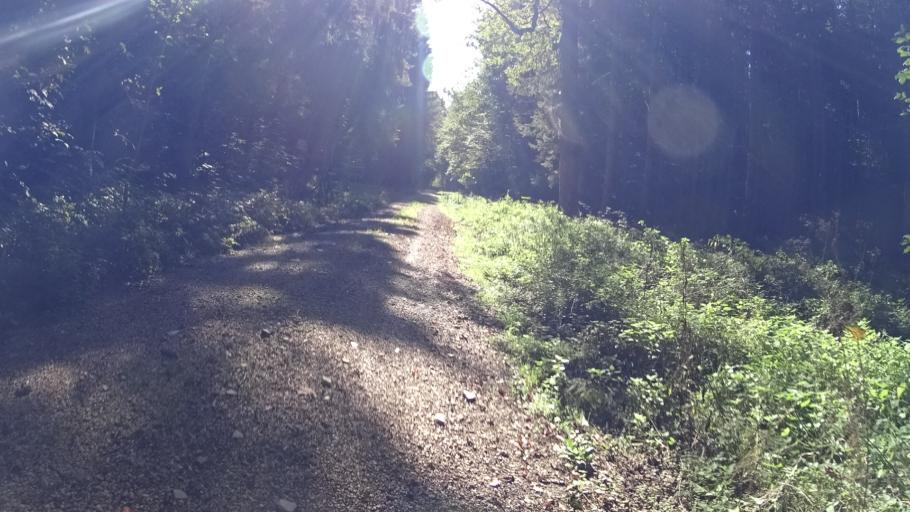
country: DE
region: Bavaria
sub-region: Upper Bavaria
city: Hitzhofen
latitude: 48.8815
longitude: 11.3061
